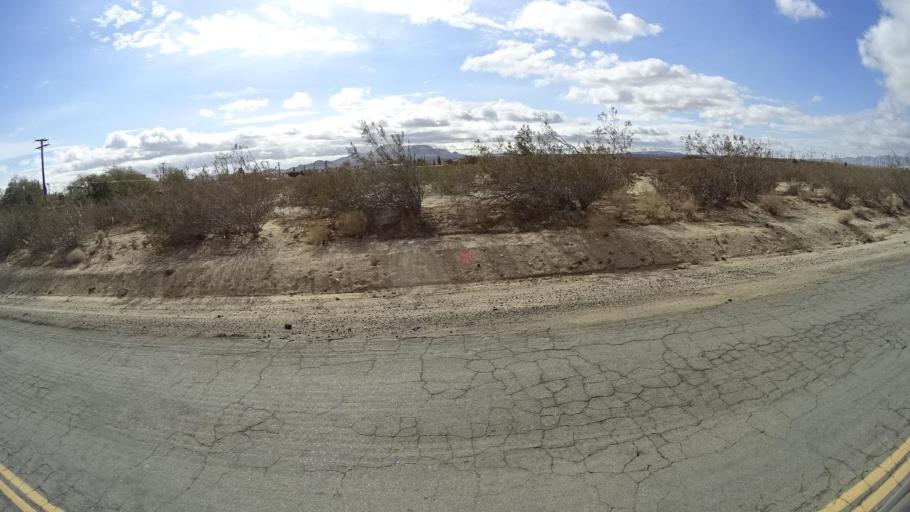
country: US
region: California
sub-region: Kern County
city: Mojave
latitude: 35.0685
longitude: -118.1841
